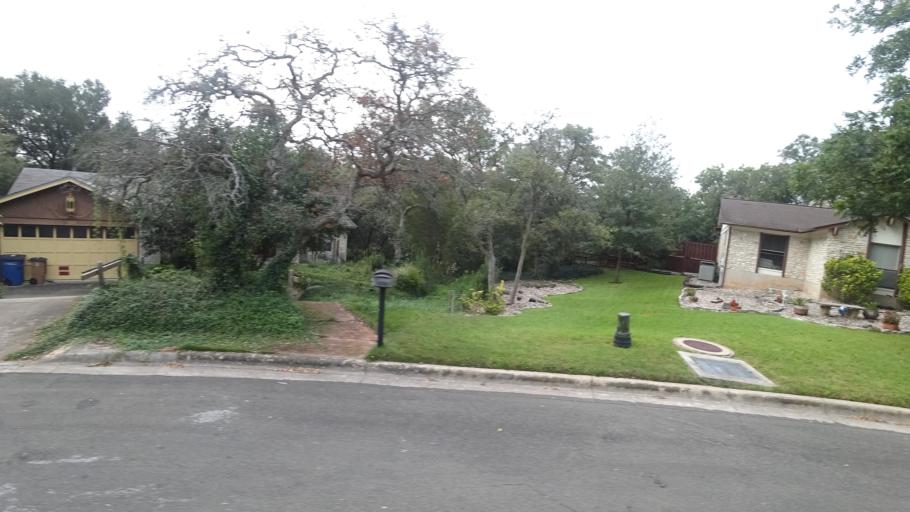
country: US
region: Texas
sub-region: Travis County
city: Wells Branch
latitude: 30.3653
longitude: -97.6646
